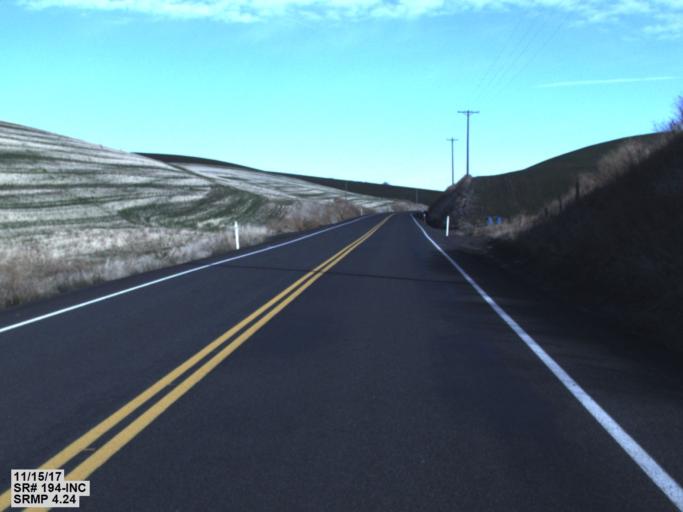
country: US
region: Washington
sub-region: Whitman County
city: Colfax
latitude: 46.7334
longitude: -117.4860
